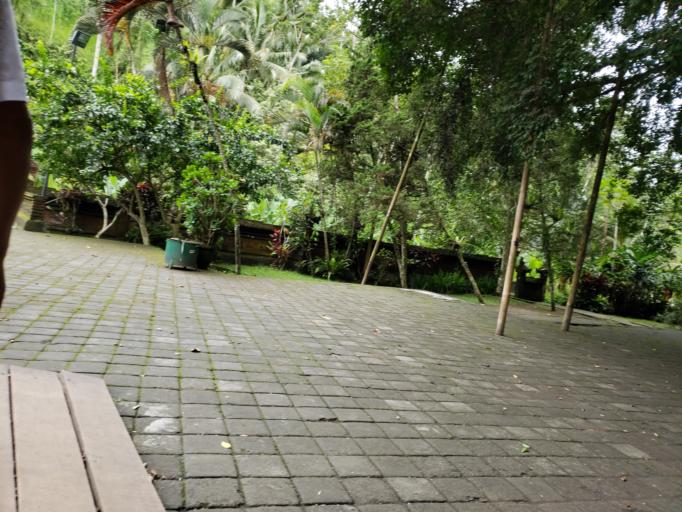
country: ID
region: Bali
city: Banjar Manukayaanyar
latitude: -8.4151
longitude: 115.3159
